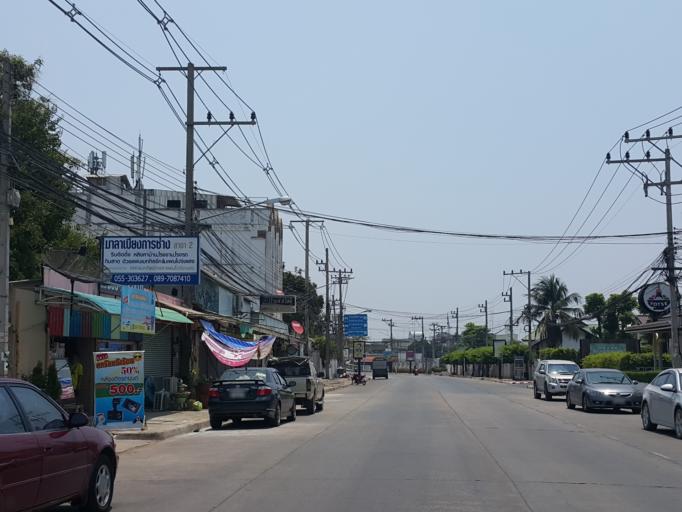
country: TH
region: Phitsanulok
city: Phitsanulok
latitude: 16.8156
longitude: 100.2580
